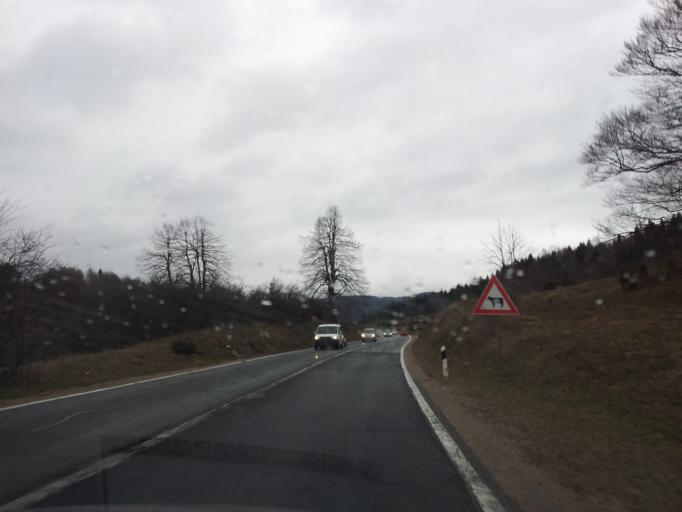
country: HR
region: Licko-Senjska
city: Jezerce
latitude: 44.8013
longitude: 15.6830
